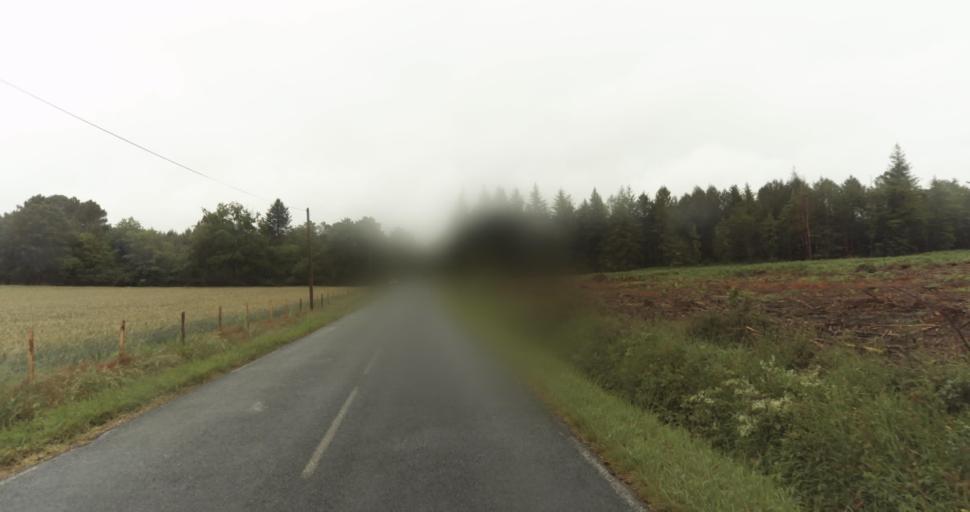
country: FR
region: Aquitaine
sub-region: Departement de la Dordogne
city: Beaumont-du-Perigord
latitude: 44.7904
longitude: 0.8450
